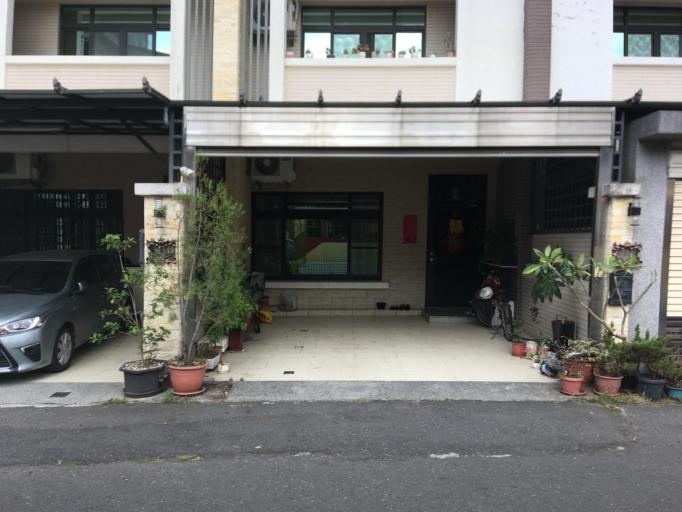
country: TW
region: Taiwan
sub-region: Chiayi
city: Jiayi Shi
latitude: 23.4908
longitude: 120.5050
